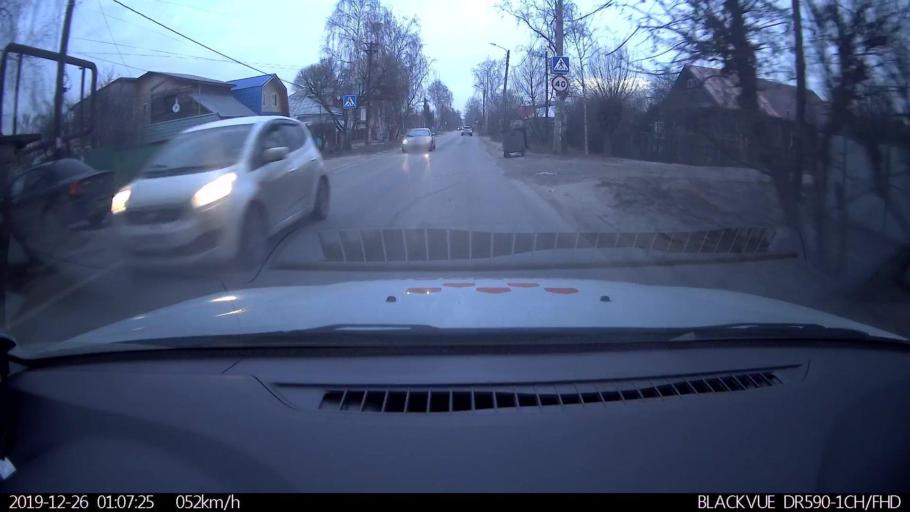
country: RU
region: Nizjnij Novgorod
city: Nizhniy Novgorod
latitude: 56.2815
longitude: 43.9092
